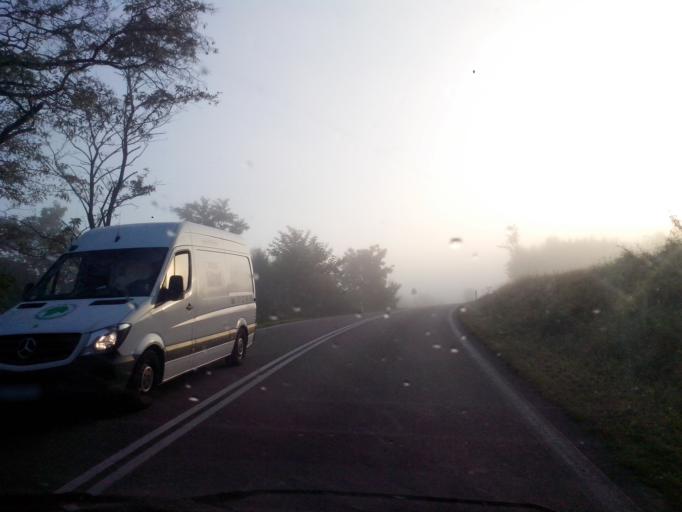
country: PL
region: Subcarpathian Voivodeship
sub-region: Powiat brzozowski
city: Domaradz
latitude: 49.8041
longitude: 21.9545
